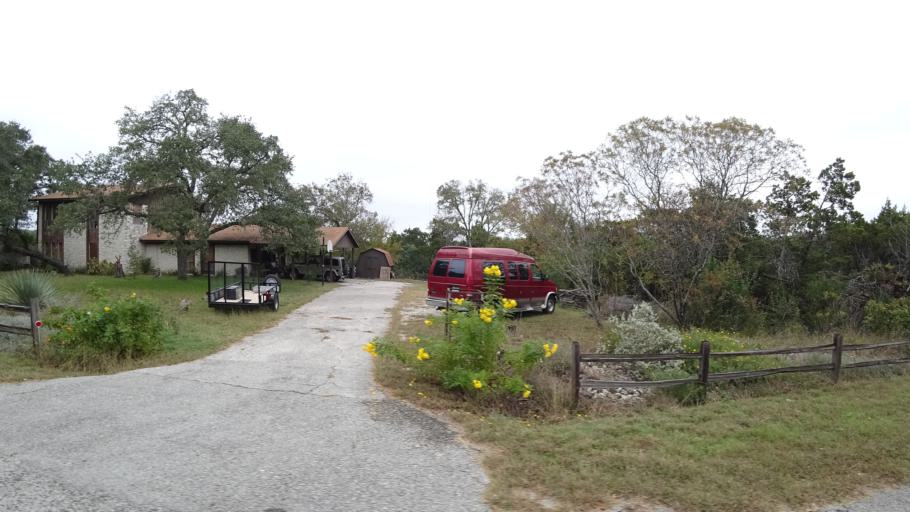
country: US
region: Texas
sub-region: Travis County
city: Barton Creek
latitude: 30.2409
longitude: -97.9066
